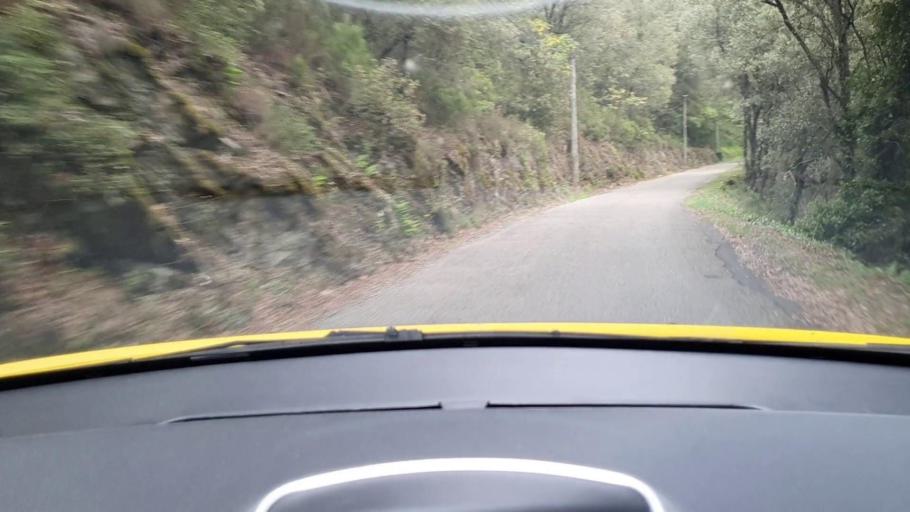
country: FR
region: Languedoc-Roussillon
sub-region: Departement du Gard
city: Sumene
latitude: 44.0079
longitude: 3.6595
